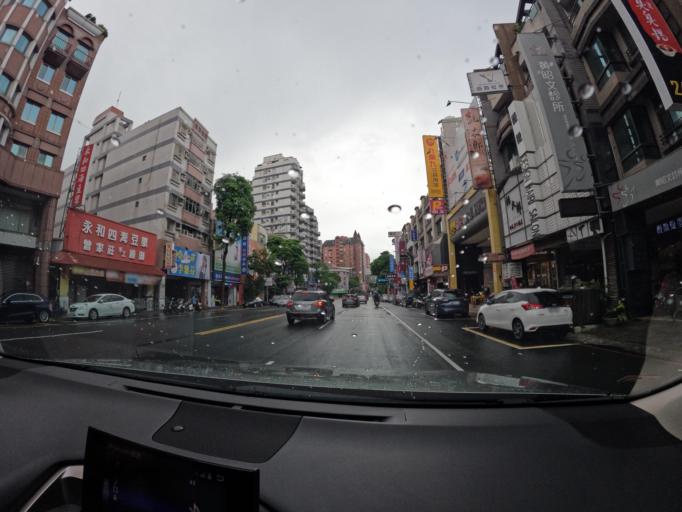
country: TW
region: Kaohsiung
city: Kaohsiung
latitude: 22.6625
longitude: 120.3084
